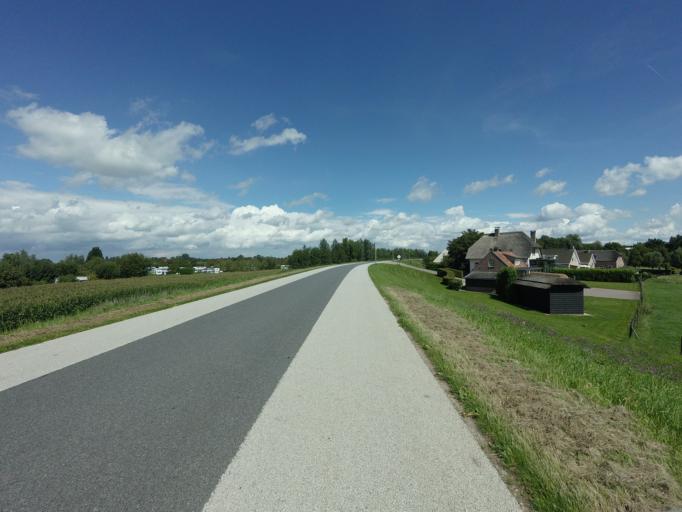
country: NL
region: Utrecht
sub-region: Gemeente Lopik
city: Lopik
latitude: 51.9582
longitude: 4.9397
